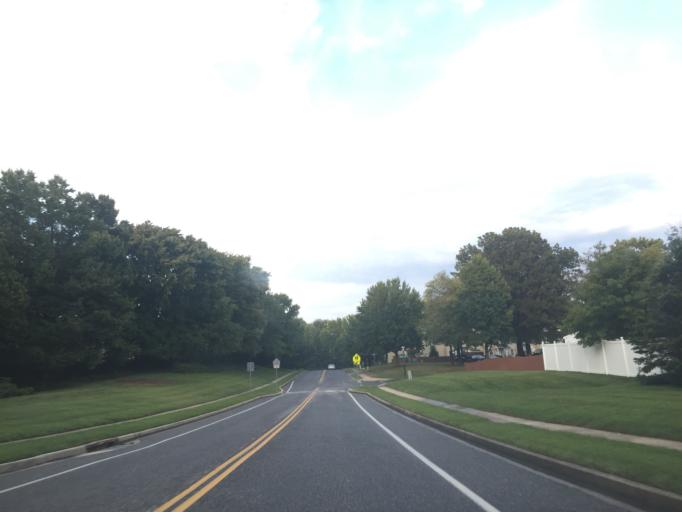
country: US
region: Maryland
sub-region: Harford County
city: Riverside
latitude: 39.4723
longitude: -76.2476
